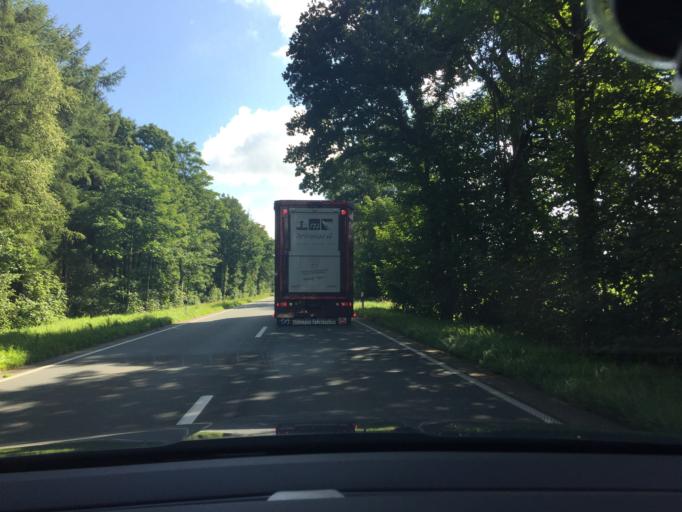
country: DE
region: Lower Saxony
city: Wittmund
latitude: 53.5647
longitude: 7.7255
